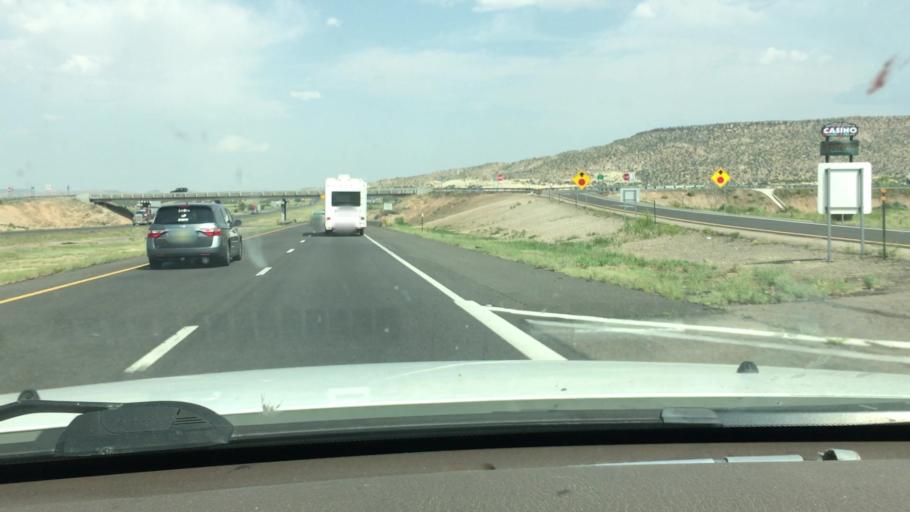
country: US
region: New Mexico
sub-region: Cibola County
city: Laguna
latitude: 35.0343
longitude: -107.4756
